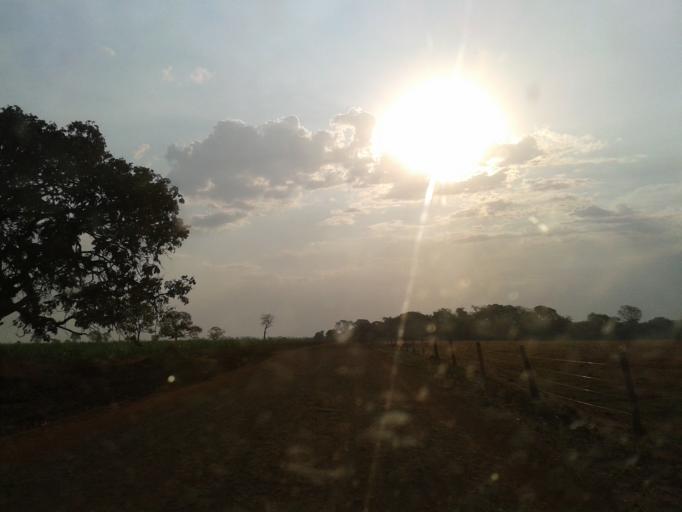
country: BR
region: Minas Gerais
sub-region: Capinopolis
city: Capinopolis
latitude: -18.7561
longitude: -49.7070
